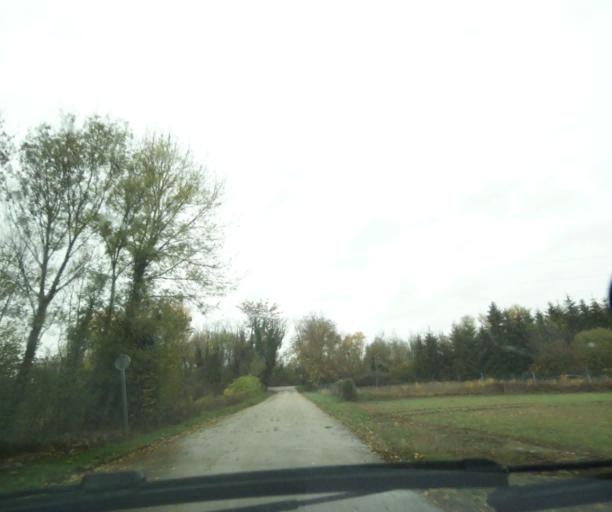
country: FR
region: Rhone-Alpes
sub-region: Departement de l'Ain
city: Saint-Jean-de-Niost
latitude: 45.8126
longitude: 5.2190
